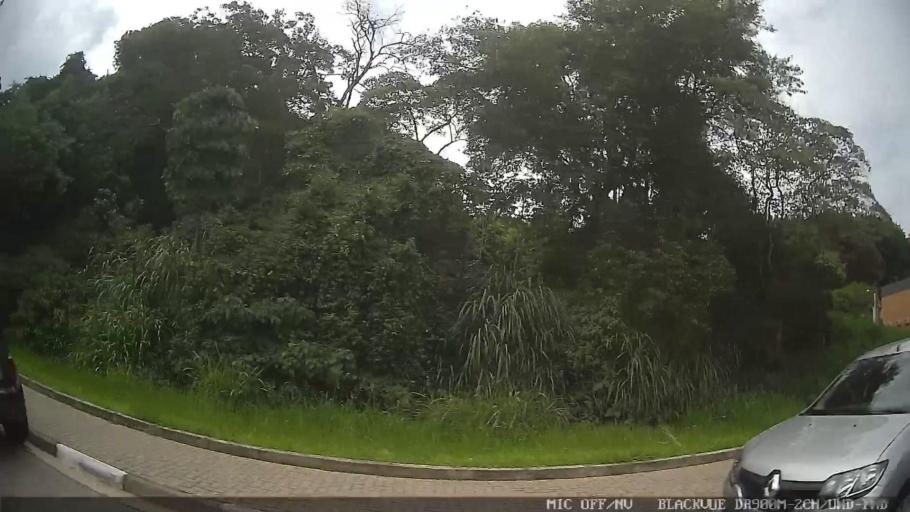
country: BR
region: Sao Paulo
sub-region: Atibaia
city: Atibaia
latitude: -23.1202
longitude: -46.5534
